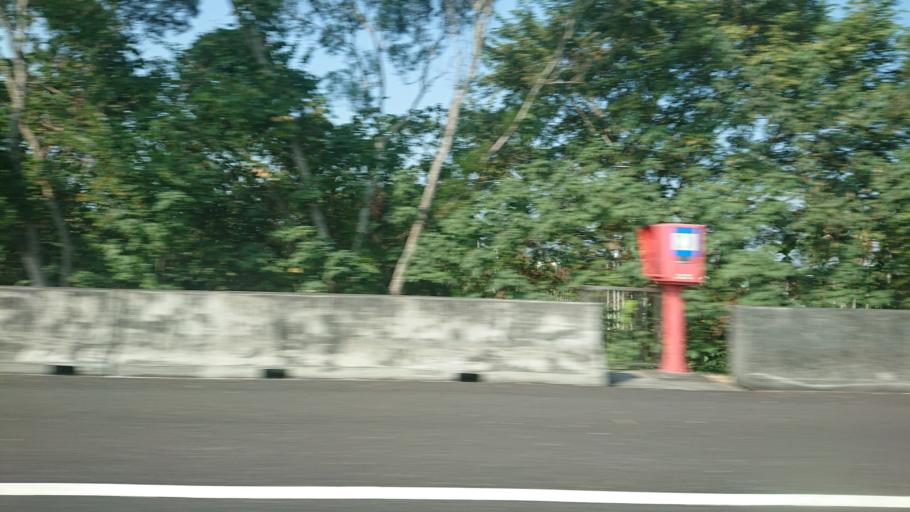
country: TW
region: Taiwan
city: Lugu
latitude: 23.8259
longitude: 120.7078
